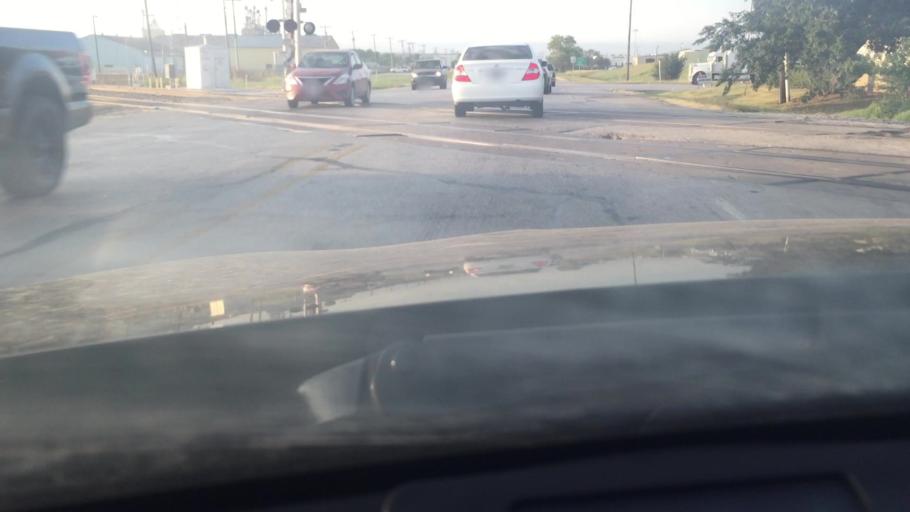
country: US
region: Texas
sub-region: Tarrant County
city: Blue Mound
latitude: 32.8376
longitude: -97.3431
